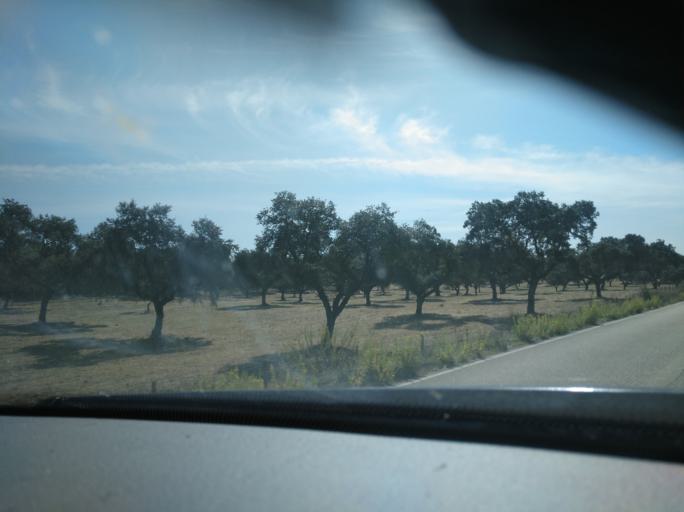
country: PT
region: Evora
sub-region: Arraiolos
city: Arraiolos
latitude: 38.6782
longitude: -8.0932
